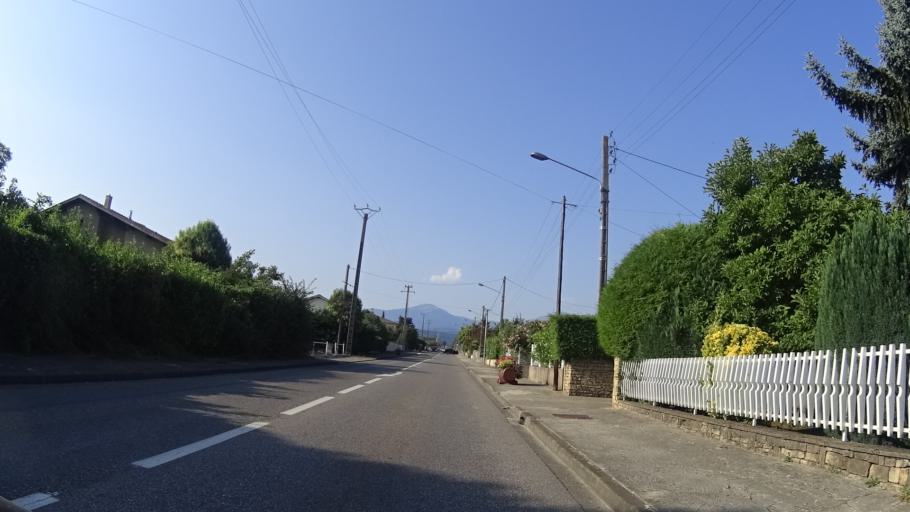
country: FR
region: Midi-Pyrenees
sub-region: Departement de l'Ariege
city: Lavelanet
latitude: 42.9759
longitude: 1.8679
